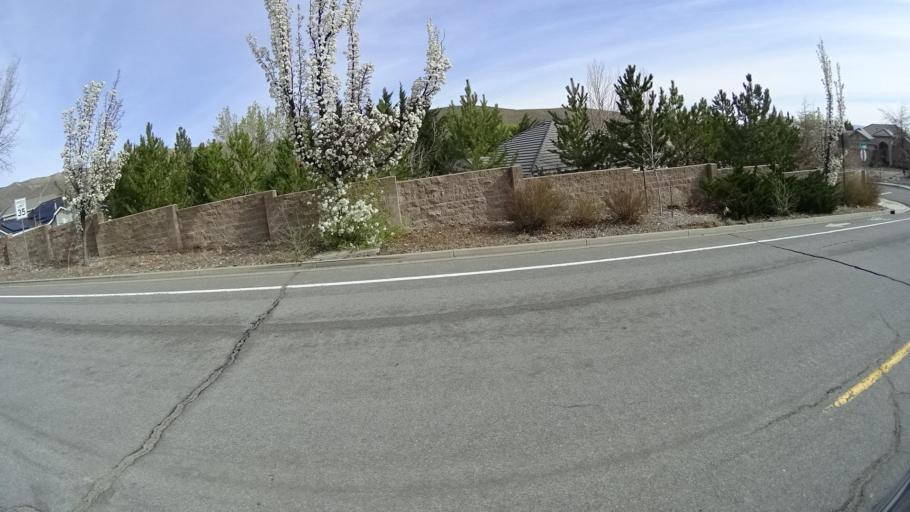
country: US
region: Nevada
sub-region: Washoe County
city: Mogul
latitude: 39.5428
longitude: -119.8740
